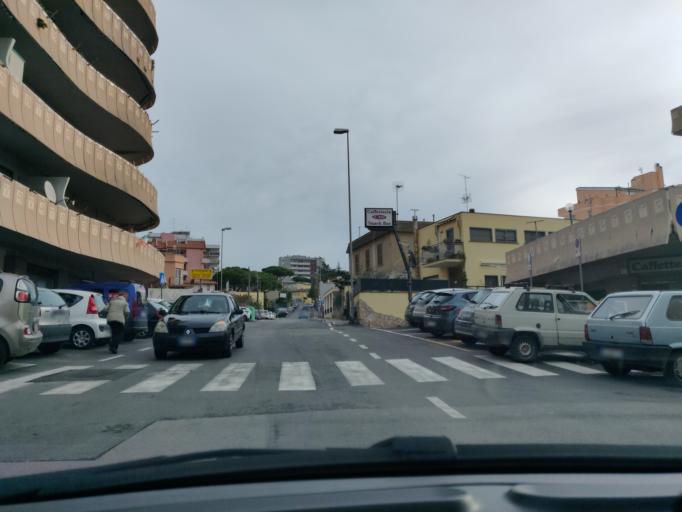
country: IT
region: Latium
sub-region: Citta metropolitana di Roma Capitale
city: Civitavecchia
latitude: 42.0964
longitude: 11.8117
